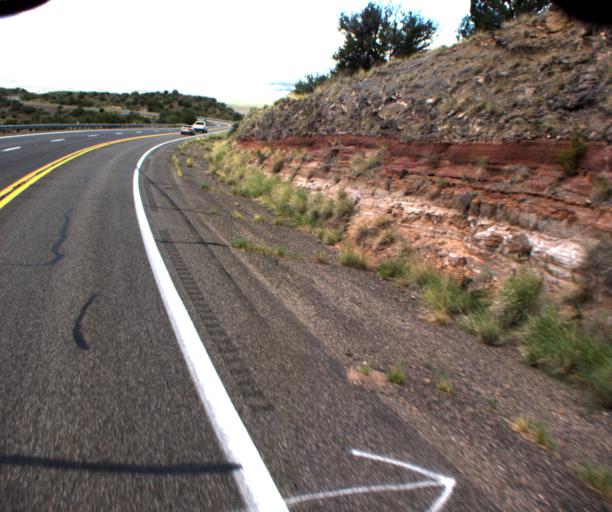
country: US
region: Arizona
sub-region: Yavapai County
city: Lake Montezuma
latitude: 34.5014
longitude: -111.7215
